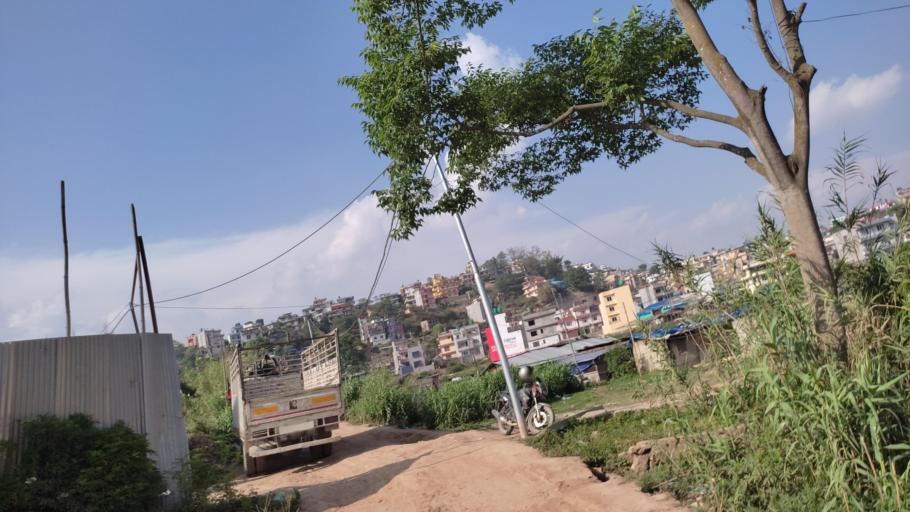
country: NP
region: Central Region
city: Kirtipur
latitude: 27.6802
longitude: 85.2625
